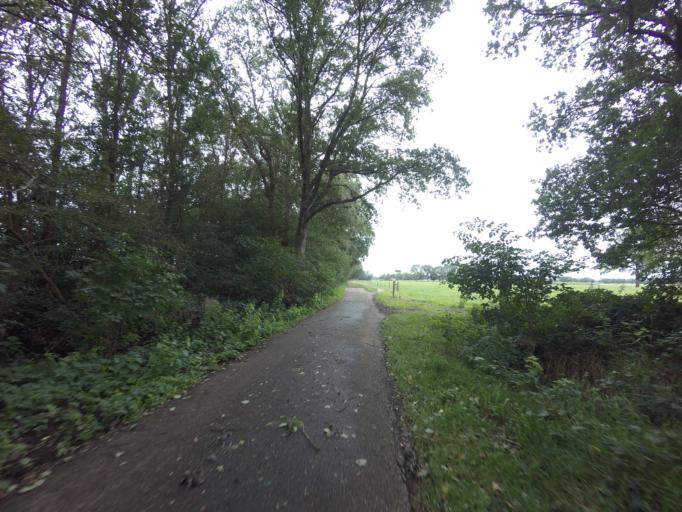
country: NL
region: Friesland
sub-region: Gemeente Weststellingwerf
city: Steggerda
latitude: 52.8902
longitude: 6.0923
